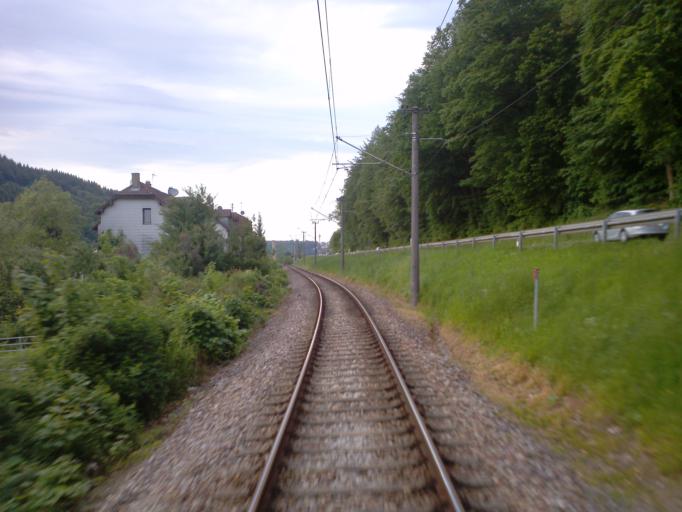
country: DE
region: Baden-Wuerttemberg
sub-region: Karlsruhe Region
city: Ettlingen
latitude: 48.9067
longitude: 8.4545
